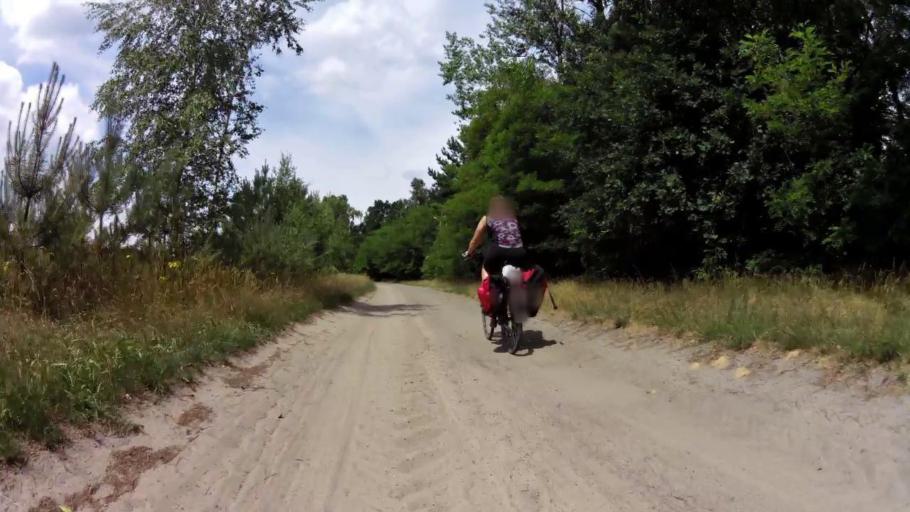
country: PL
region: West Pomeranian Voivodeship
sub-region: Powiat lobeski
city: Lobez
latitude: 53.5463
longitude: 15.6775
